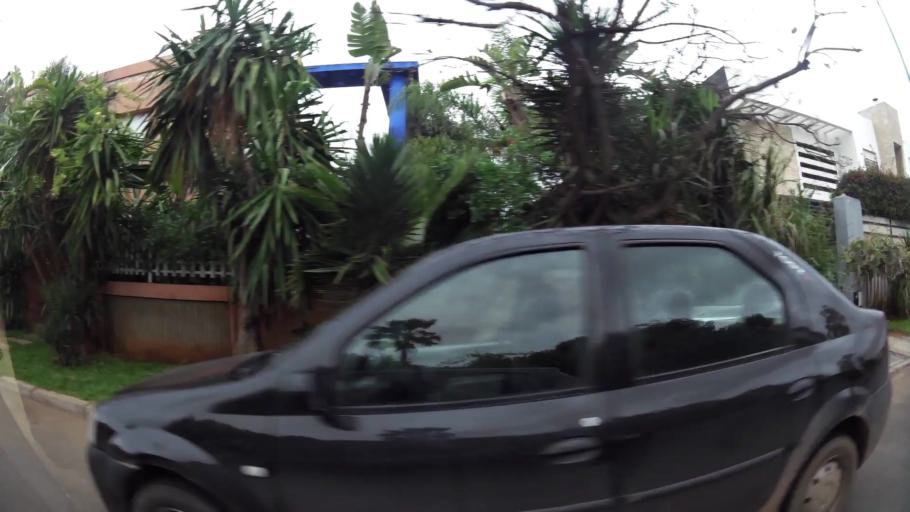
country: MA
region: Grand Casablanca
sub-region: Casablanca
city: Casablanca
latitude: 33.5420
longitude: -7.6368
